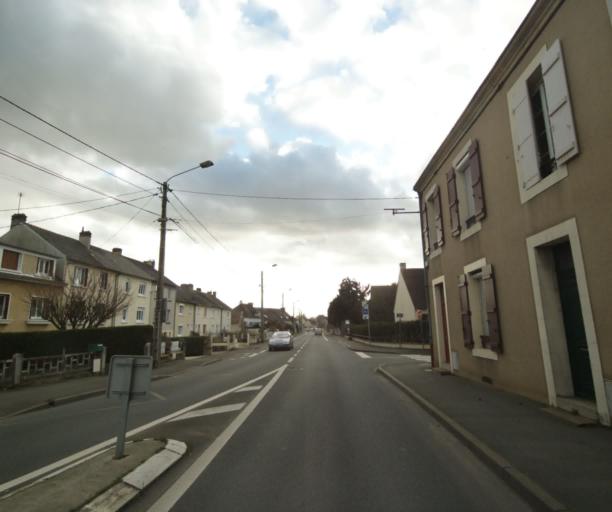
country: FR
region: Pays de la Loire
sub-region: Departement de la Sarthe
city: Allonnes
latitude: 47.9896
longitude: 0.1675
